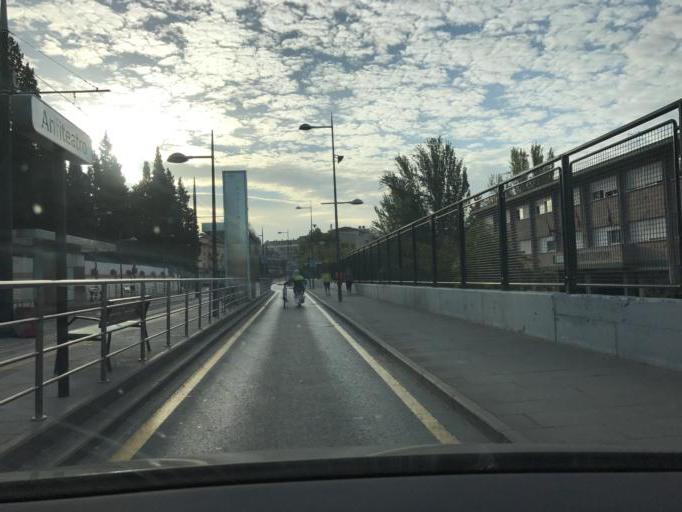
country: ES
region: Andalusia
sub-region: Provincia de Granada
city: Maracena
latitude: 37.2112
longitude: -3.6345
